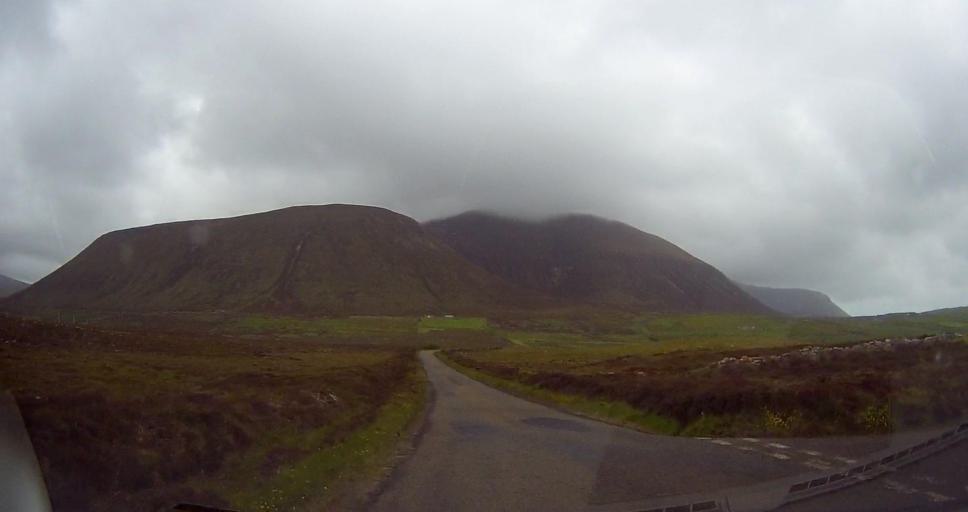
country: GB
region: Scotland
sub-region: Orkney Islands
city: Stromness
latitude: 58.9039
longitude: -3.3020
